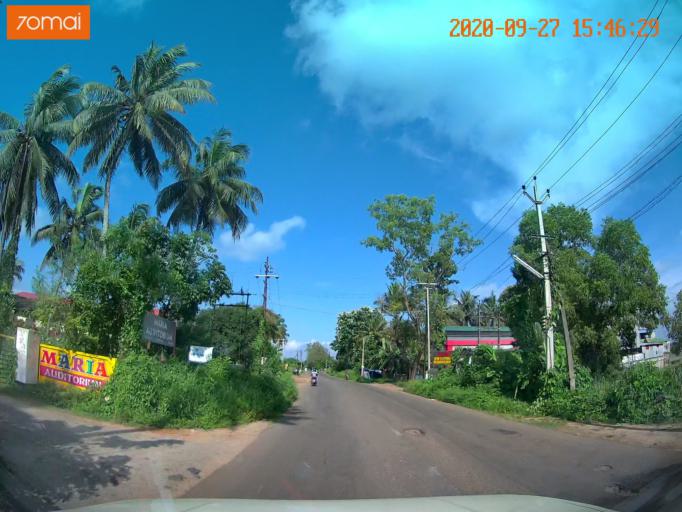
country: IN
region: Kerala
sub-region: Thrissur District
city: Thanniyam
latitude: 10.4803
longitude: 76.1215
